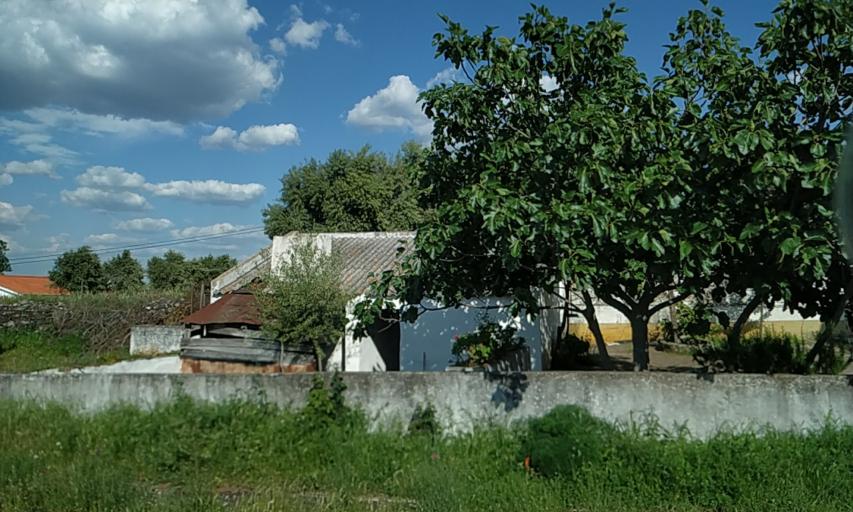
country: PT
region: Evora
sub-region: Estremoz
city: Estremoz
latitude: 38.8667
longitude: -7.5688
